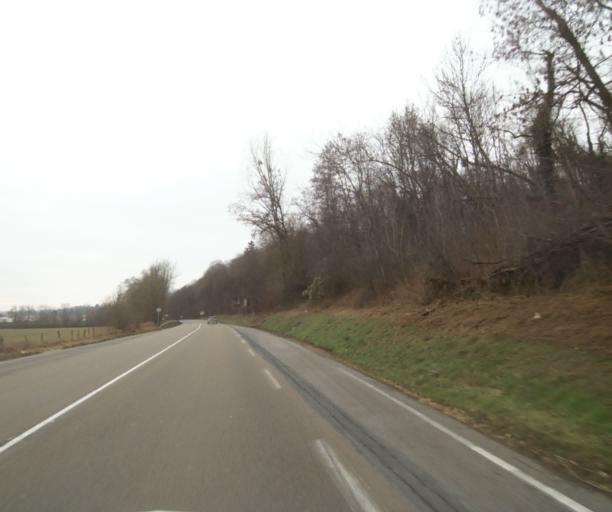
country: FR
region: Champagne-Ardenne
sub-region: Departement de la Haute-Marne
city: Bienville
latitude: 48.5956
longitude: 5.0308
